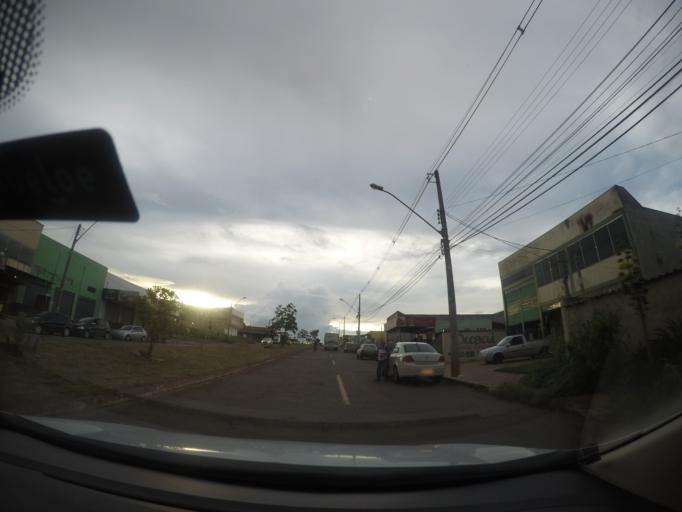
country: BR
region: Goias
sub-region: Goiania
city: Goiania
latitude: -16.7339
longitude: -49.3603
